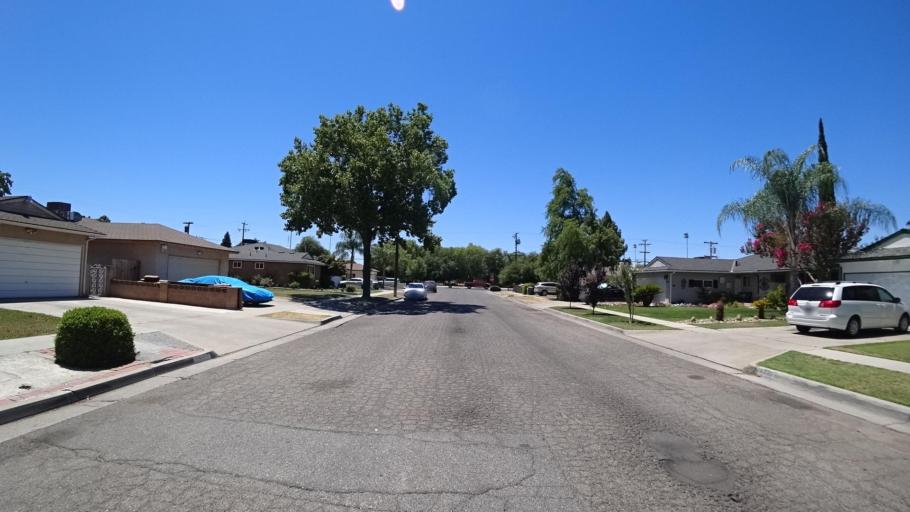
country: US
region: California
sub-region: Fresno County
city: Fresno
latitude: 36.8020
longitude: -119.7687
